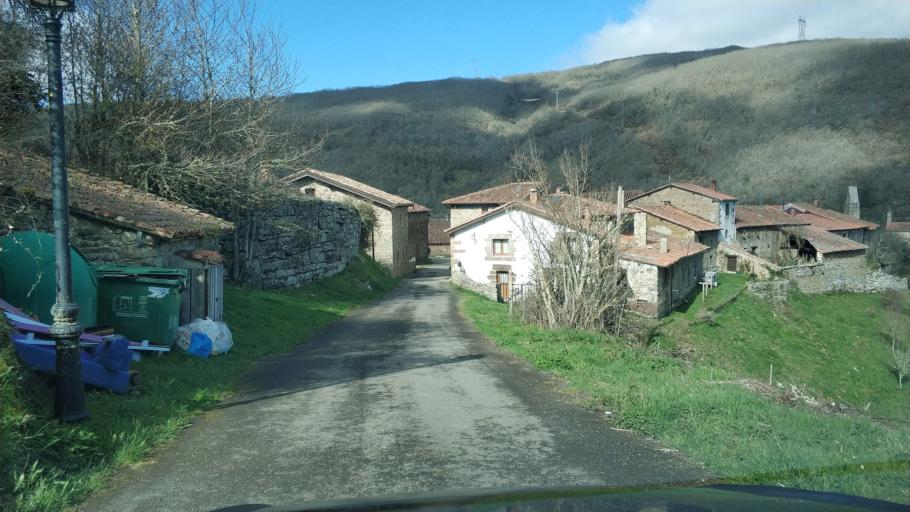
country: ES
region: Castille and Leon
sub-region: Provincia de Burgos
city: Arija
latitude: 42.9057
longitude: -4.0290
